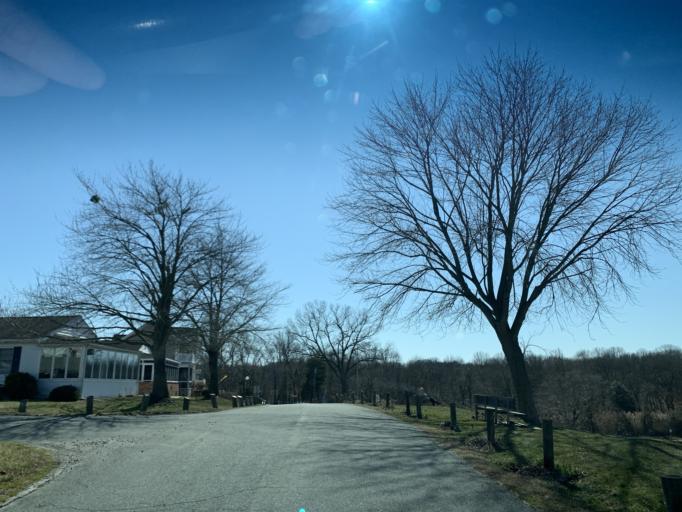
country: US
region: Maryland
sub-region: Cecil County
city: Charlestown
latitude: 39.4377
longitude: -75.9781
